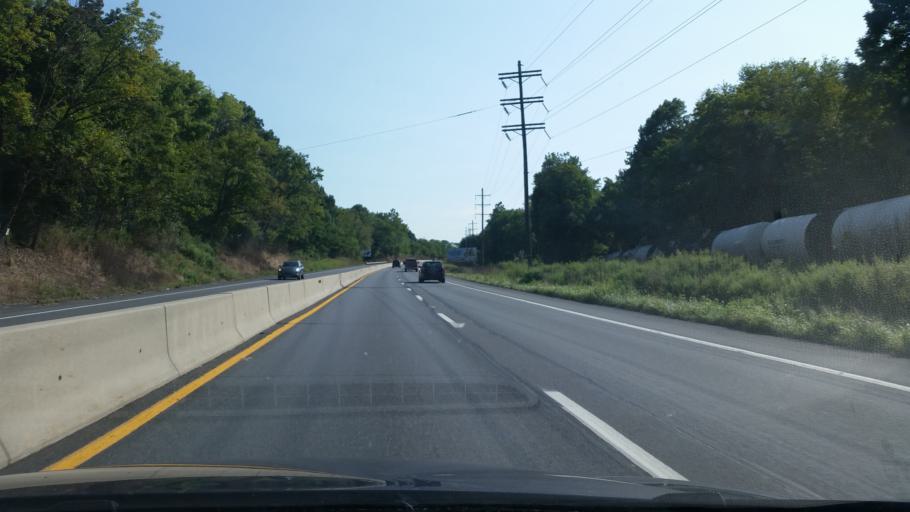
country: US
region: Pennsylvania
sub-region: Berks County
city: Shoemakersville
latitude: 40.4820
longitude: -75.9645
